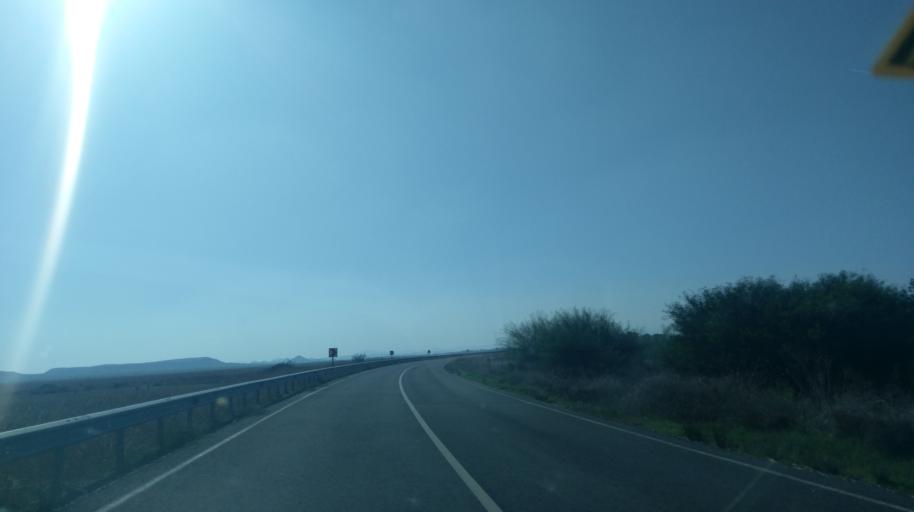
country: CY
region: Larnaka
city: Athienou
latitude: 35.1247
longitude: 33.5222
